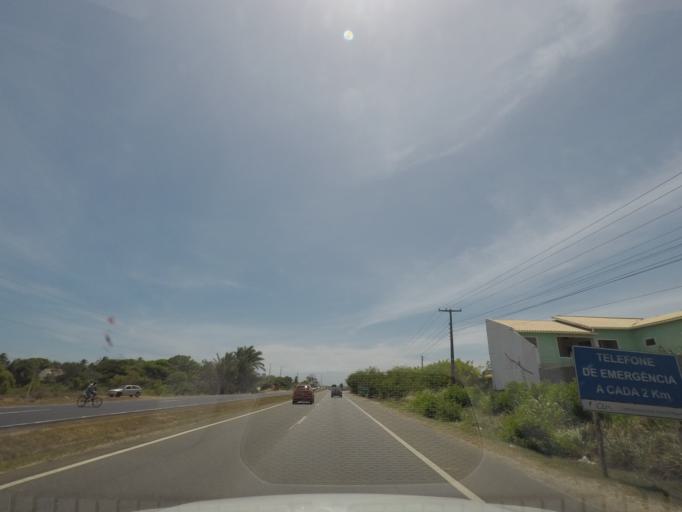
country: BR
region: Bahia
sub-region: Camacari
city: Camacari
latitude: -12.7116
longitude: -38.1448
